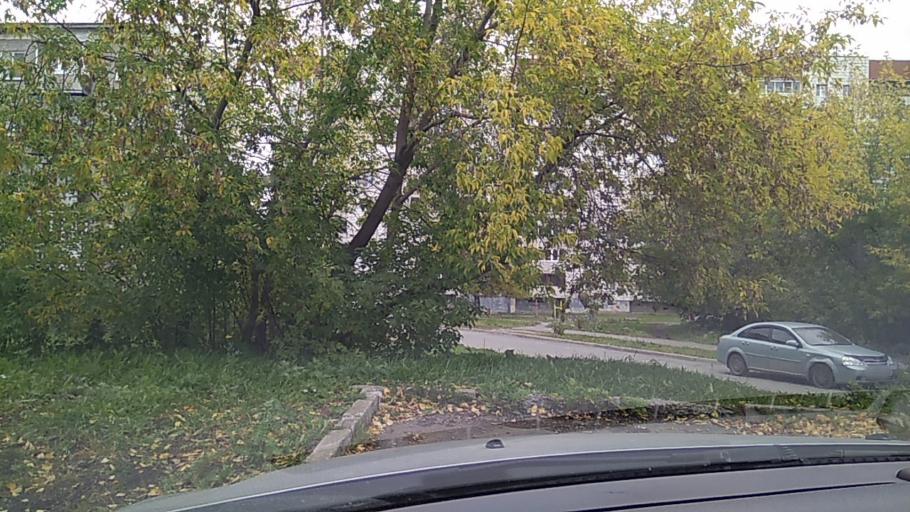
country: RU
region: Sverdlovsk
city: Yekaterinburg
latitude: 56.8291
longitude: 60.5556
